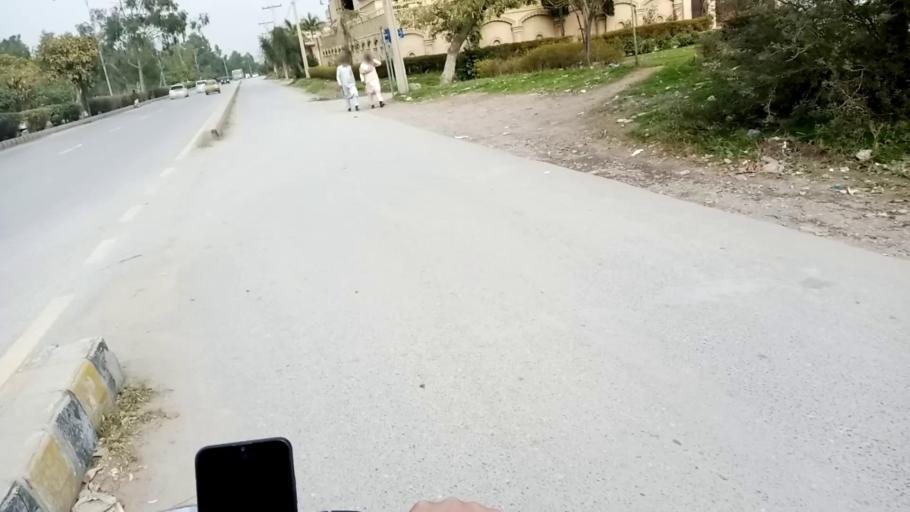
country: PK
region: Khyber Pakhtunkhwa
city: Peshawar
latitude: 33.9652
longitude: 71.4332
